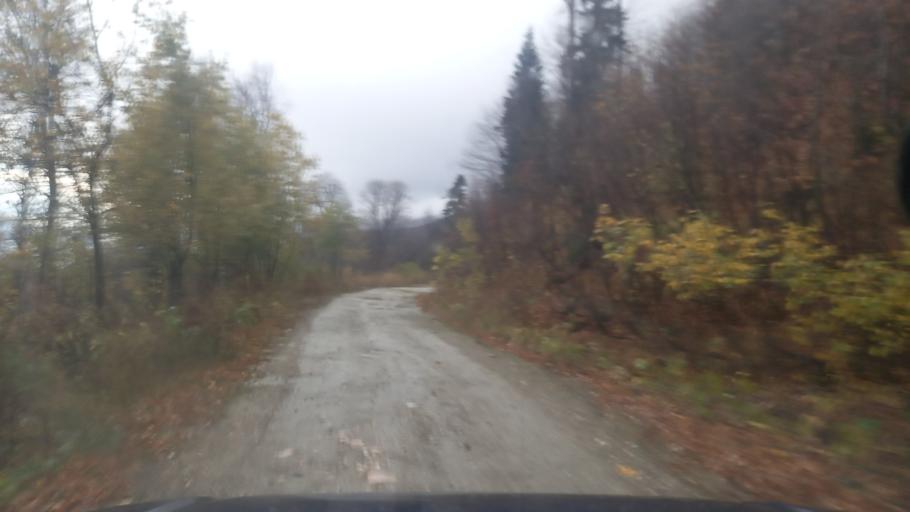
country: RU
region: Krasnodarskiy
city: Dagomys
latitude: 43.9912
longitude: 39.8538
